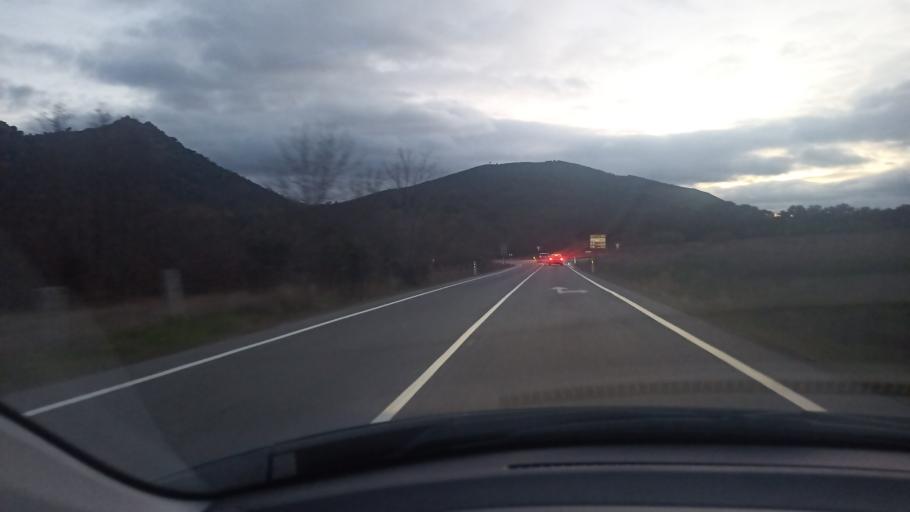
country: ES
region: Madrid
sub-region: Provincia de Madrid
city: Robledo de Chavela
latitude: 40.4725
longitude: -4.2581
